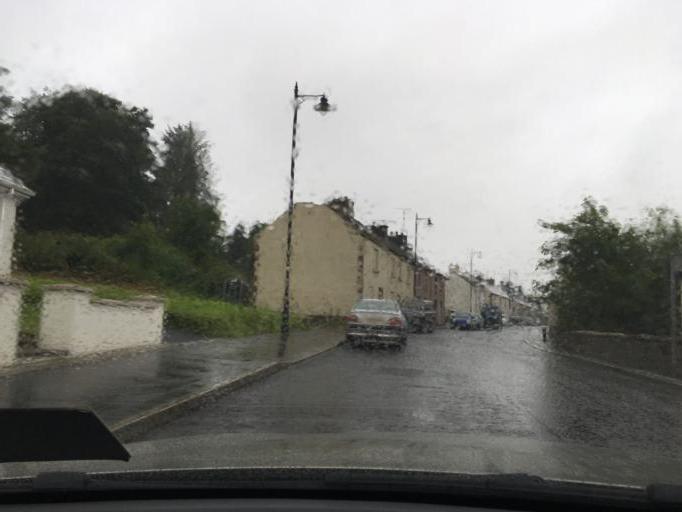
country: GB
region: Northern Ireland
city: Irvinestown
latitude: 54.5506
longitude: -7.8330
